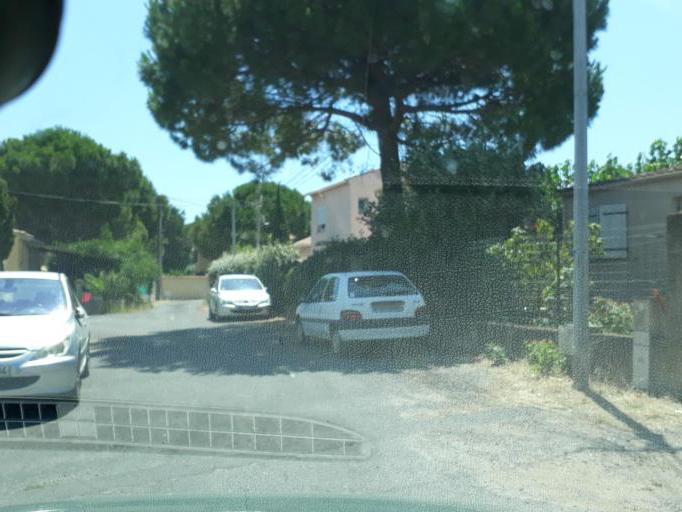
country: FR
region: Languedoc-Roussillon
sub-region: Departement de l'Herault
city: Agde
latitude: 43.2882
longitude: 3.4481
